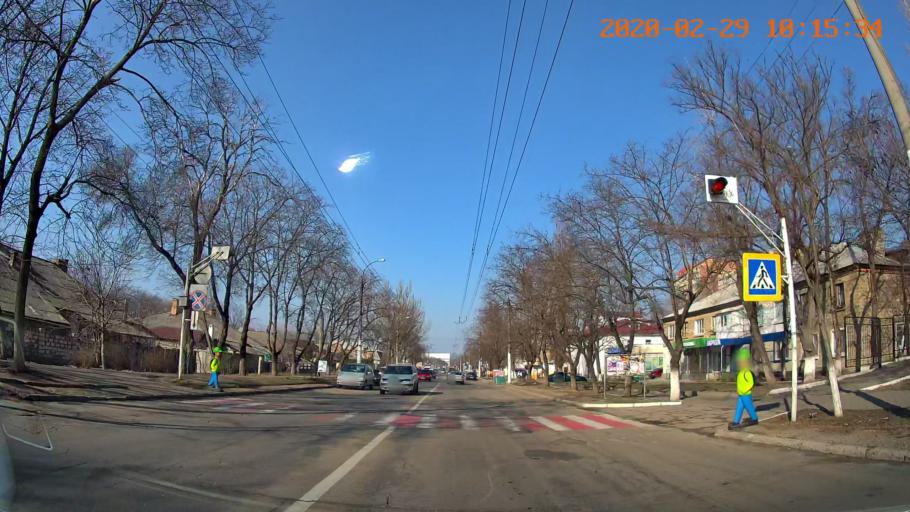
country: MD
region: Telenesti
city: Tiraspolul Nou
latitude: 46.8534
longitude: 29.6357
